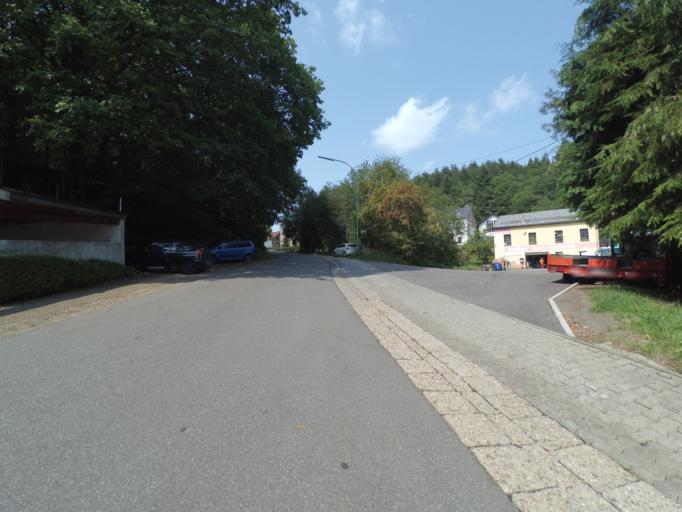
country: DE
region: Saarland
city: Britten
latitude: 49.5213
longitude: 6.6746
